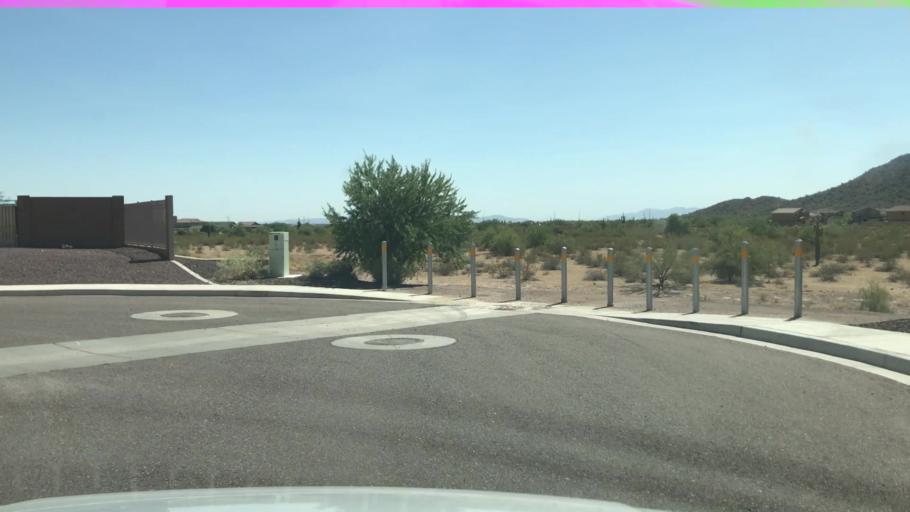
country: US
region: Arizona
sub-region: Maricopa County
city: Sun City West
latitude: 33.7298
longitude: -112.2358
